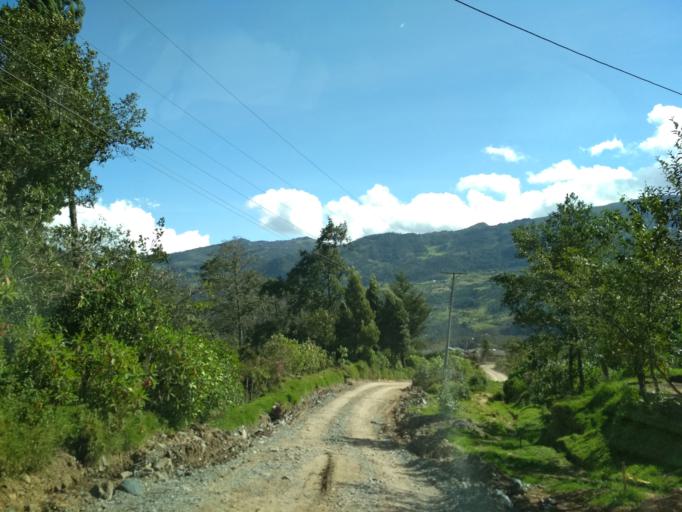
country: CO
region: Cauca
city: Jambalo
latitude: 2.7101
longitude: -76.3278
